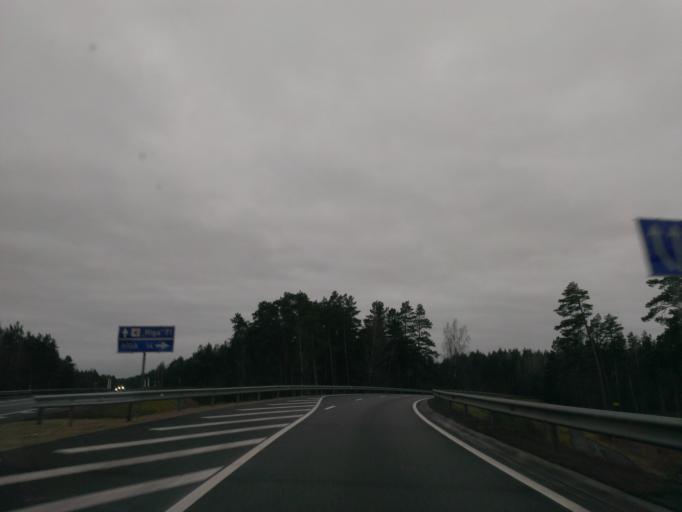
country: LV
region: Riga
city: Bergi
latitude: 57.0126
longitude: 24.3078
